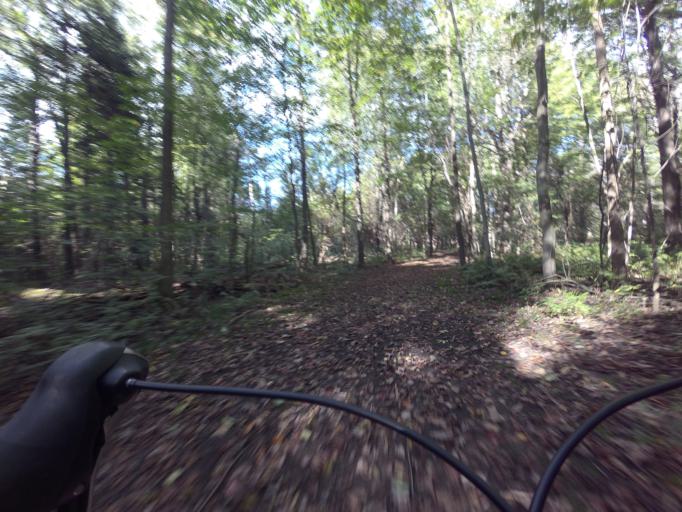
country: CA
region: Ontario
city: Bells Corners
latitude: 45.0956
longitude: -75.6302
